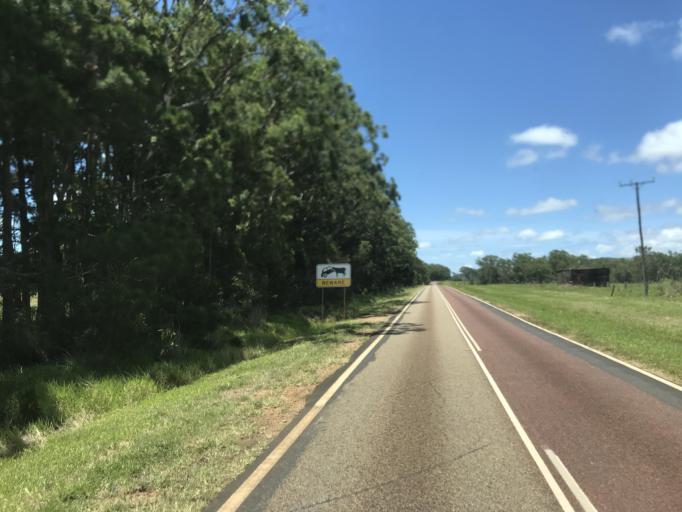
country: AU
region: Queensland
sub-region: Tablelands
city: Ravenshoe
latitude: -17.5213
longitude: 145.4522
